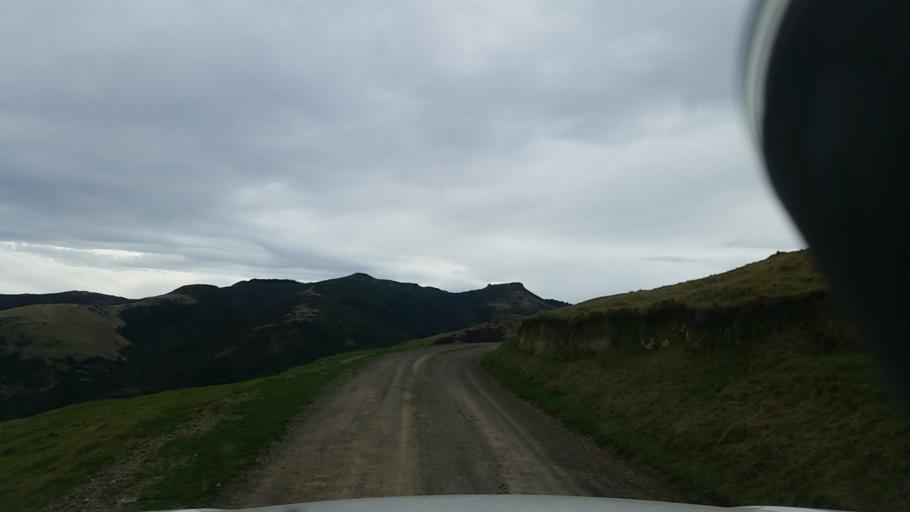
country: NZ
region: Canterbury
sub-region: Christchurch City
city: Christchurch
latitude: -43.8567
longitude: 173.0188
